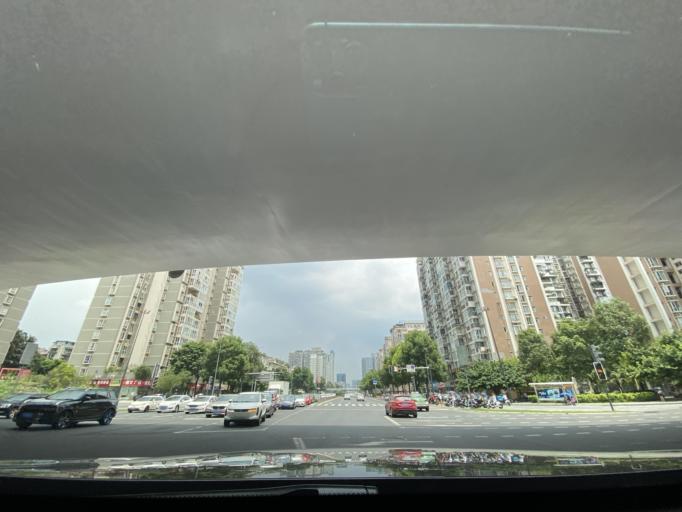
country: CN
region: Sichuan
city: Chengdu
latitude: 30.6109
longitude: 104.0749
